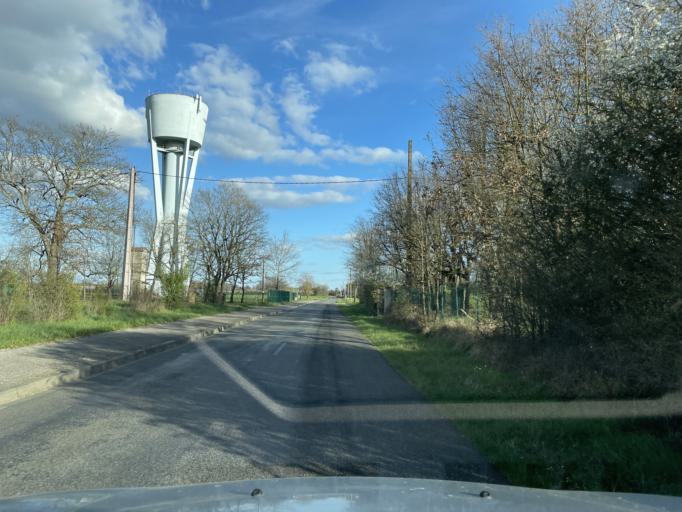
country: FR
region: Midi-Pyrenees
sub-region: Departement de la Haute-Garonne
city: Leguevin
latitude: 43.6077
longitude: 1.2155
